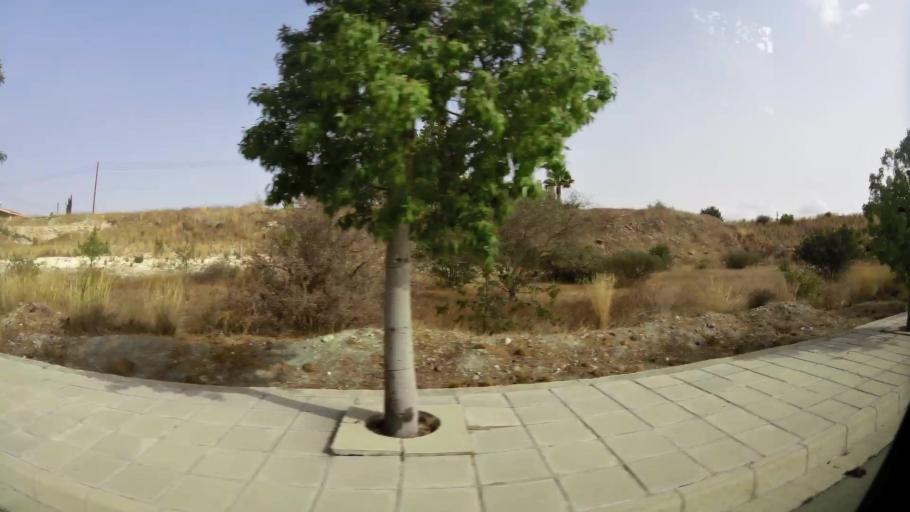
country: CY
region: Lefkosia
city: Geri
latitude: 35.0775
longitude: 33.3912
